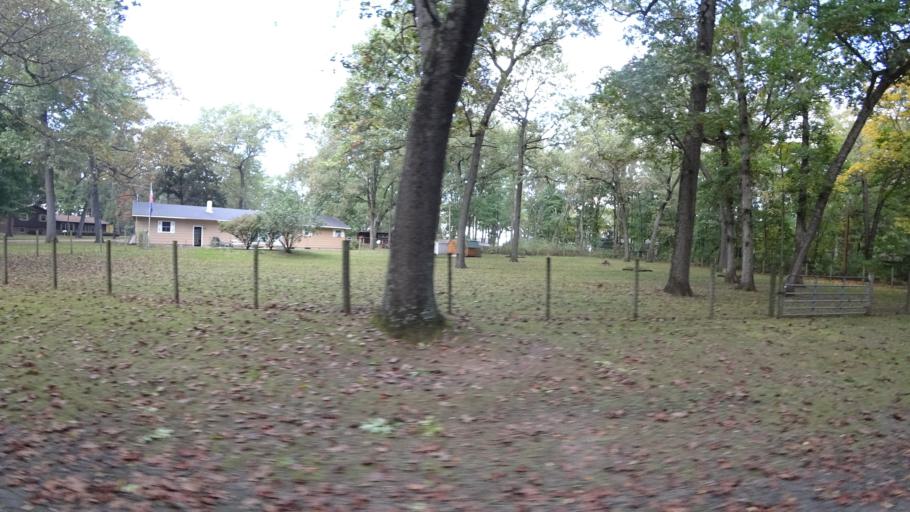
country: US
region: Michigan
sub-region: Saint Joseph County
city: Three Rivers
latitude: 41.9530
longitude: -85.5887
